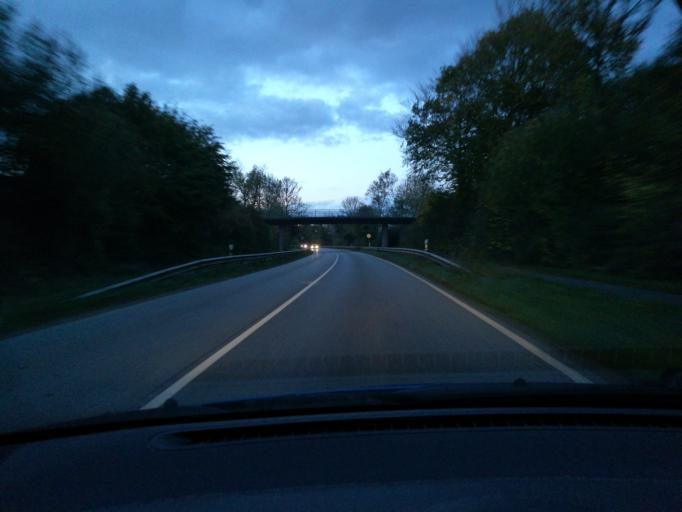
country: DE
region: Schleswig-Holstein
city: Busdorf
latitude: 54.4926
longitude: 9.5561
